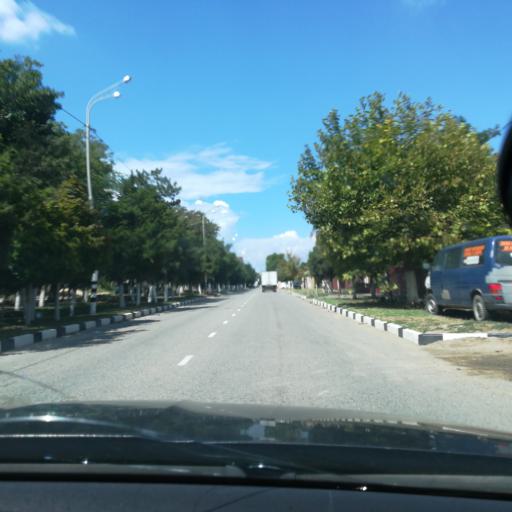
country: RU
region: Krasnodarskiy
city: Taman'
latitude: 45.2174
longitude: 36.7347
